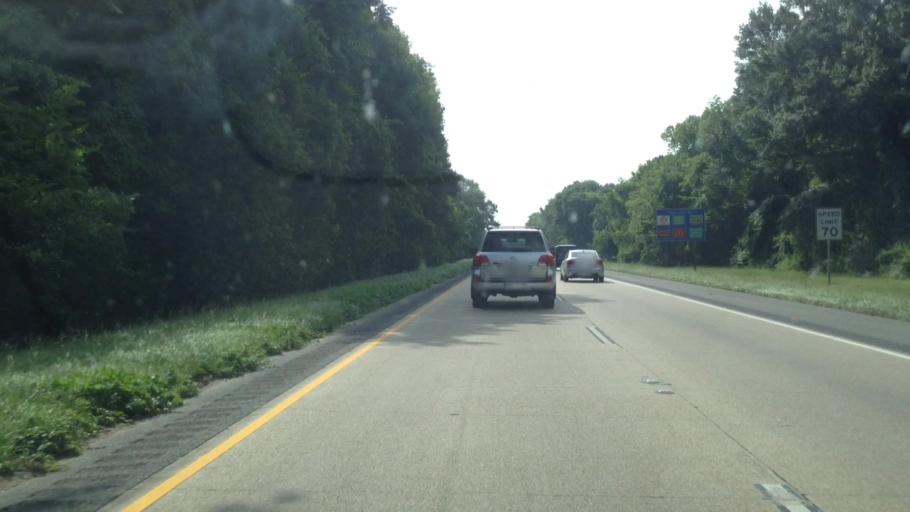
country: US
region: Louisiana
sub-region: Ascension Parish
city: Sorrento
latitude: 30.1765
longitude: -90.8881
